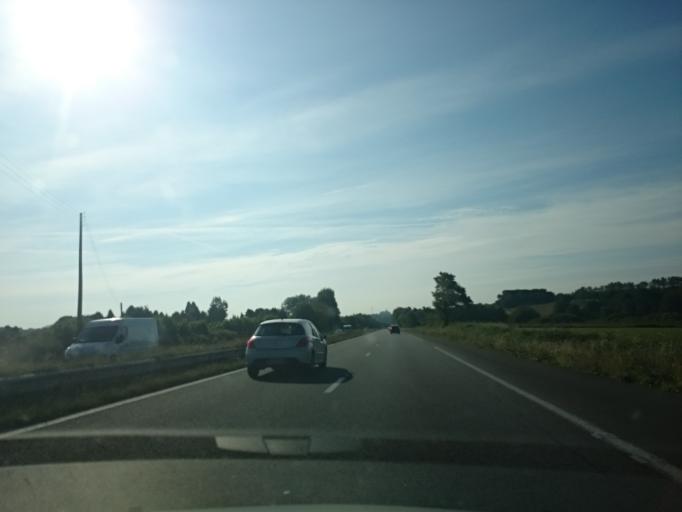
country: FR
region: Brittany
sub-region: Departement du Finistere
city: Saint-Yvi
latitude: 47.9424
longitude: -3.9271
